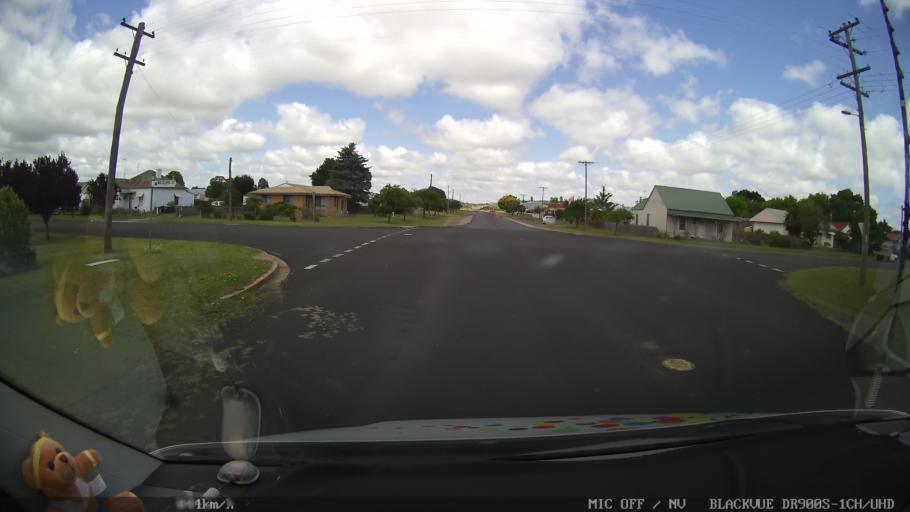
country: AU
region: New South Wales
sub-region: Glen Innes Severn
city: Glen Innes
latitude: -29.7301
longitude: 151.7328
